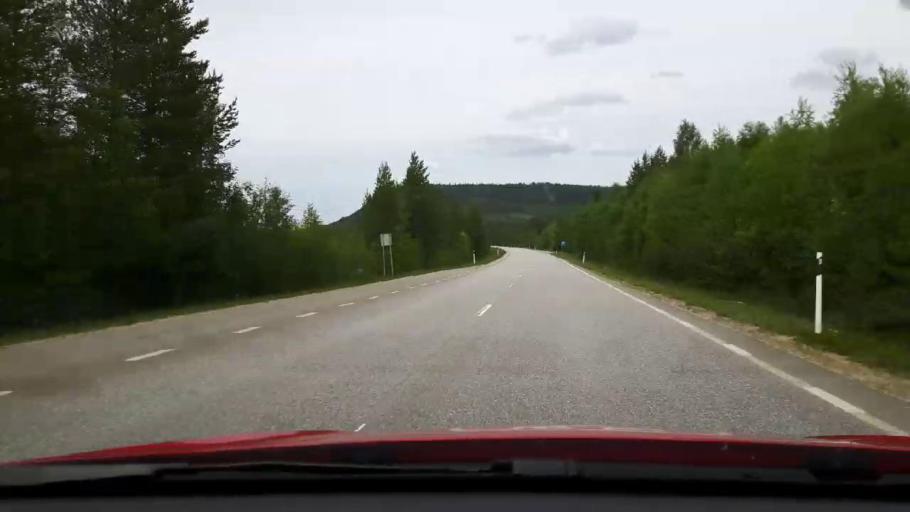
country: SE
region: Jaemtland
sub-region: Harjedalens Kommun
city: Sveg
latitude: 62.0895
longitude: 14.2471
